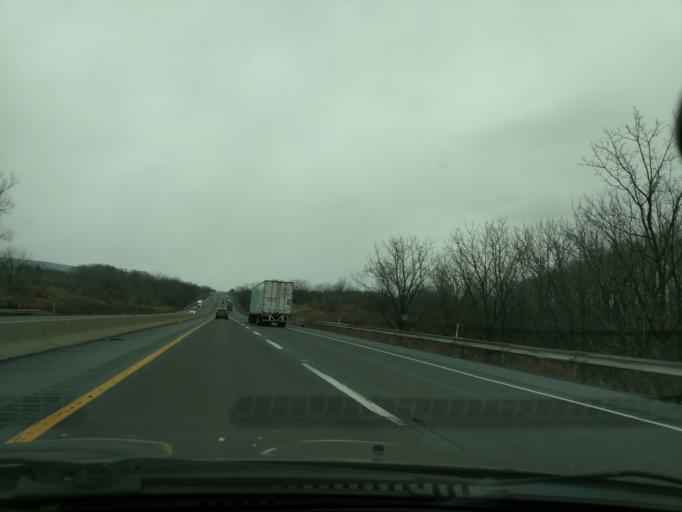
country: US
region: Pennsylvania
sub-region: Berks County
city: West Hamburg
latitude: 40.5421
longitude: -76.0377
